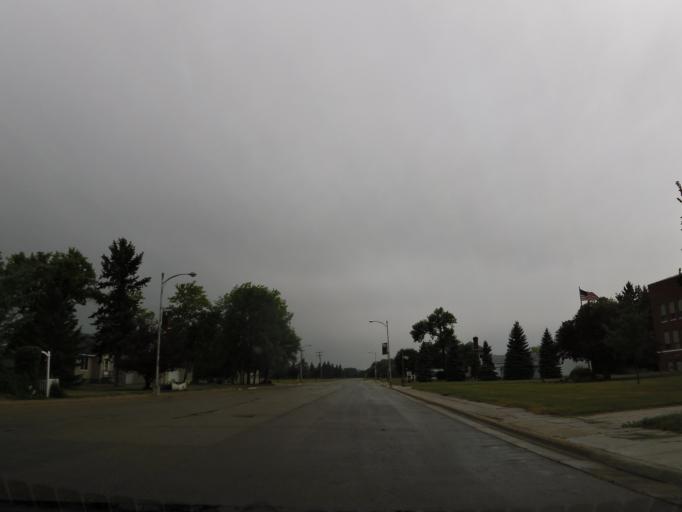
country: US
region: Minnesota
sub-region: Marshall County
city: Warren
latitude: 48.4497
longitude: -96.8783
